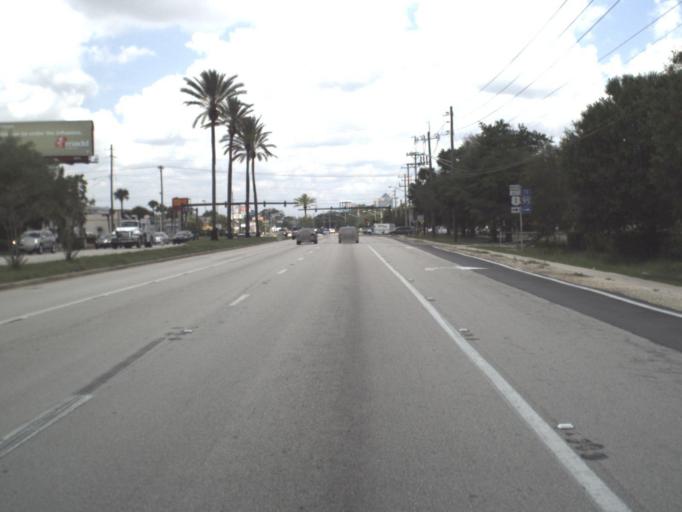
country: US
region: Florida
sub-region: Duval County
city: Jacksonville
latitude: 30.2862
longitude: -81.6324
